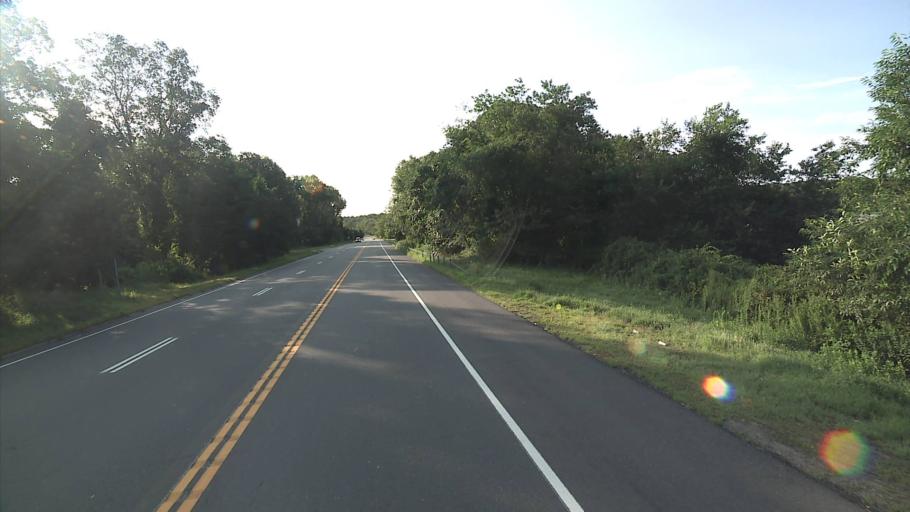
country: US
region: Connecticut
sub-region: New London County
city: Norwich
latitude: 41.5059
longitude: -72.0424
